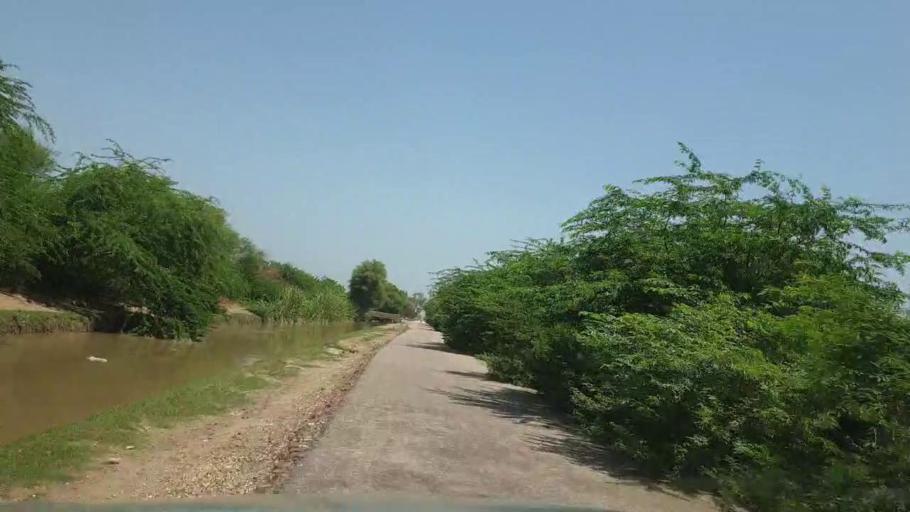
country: PK
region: Sindh
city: Rohri
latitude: 27.6276
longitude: 69.0981
